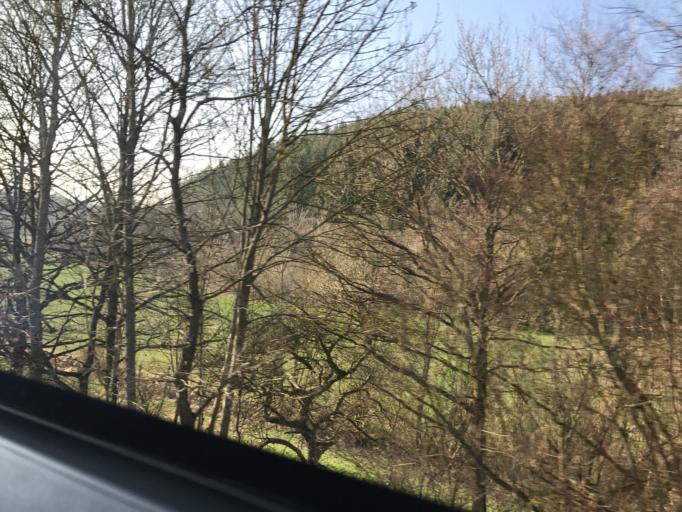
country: DE
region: Rheinland-Pfalz
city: Callbach
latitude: 49.7011
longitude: 7.7124
